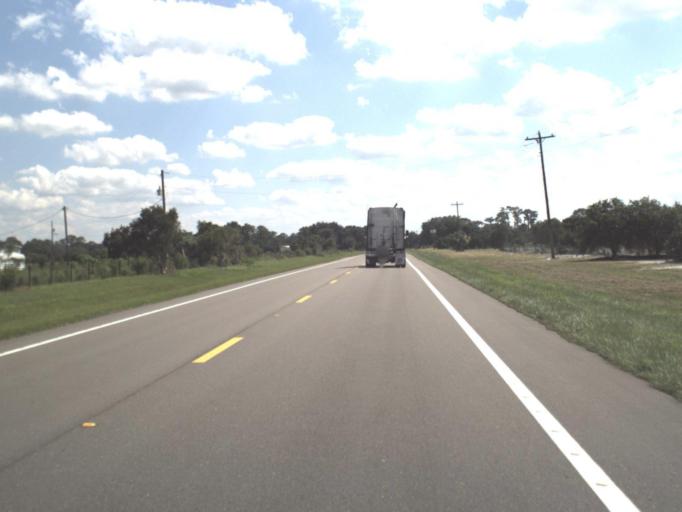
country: US
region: Florida
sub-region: Hardee County
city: Zolfo Springs
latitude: 27.4678
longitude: -81.7064
